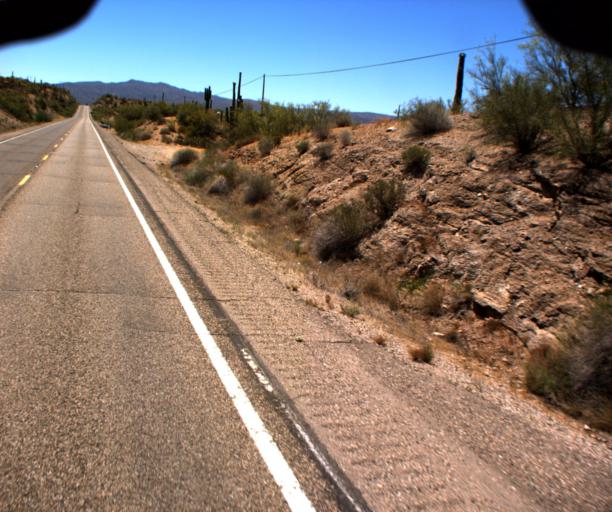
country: US
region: Arizona
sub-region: Pinal County
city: Kearny
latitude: 33.0910
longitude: -110.9297
